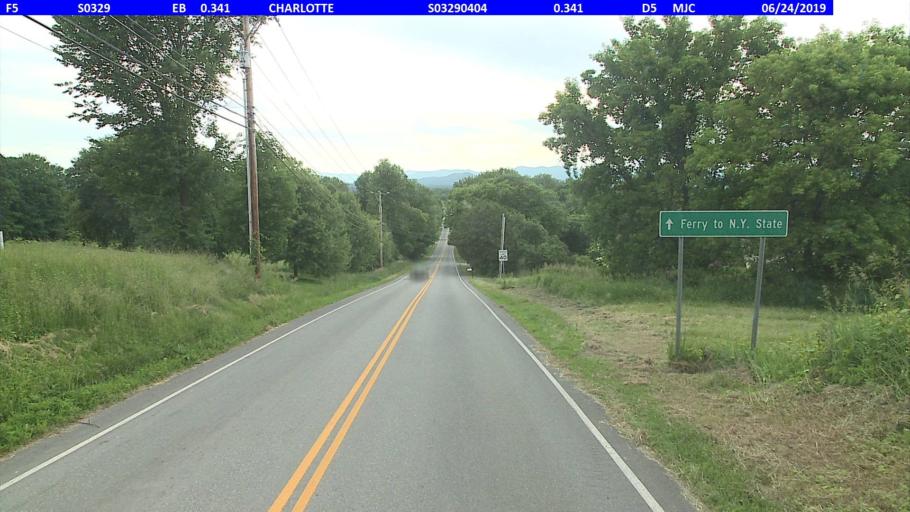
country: US
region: Vermont
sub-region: Addison County
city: Vergennes
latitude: 44.3106
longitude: -73.2535
